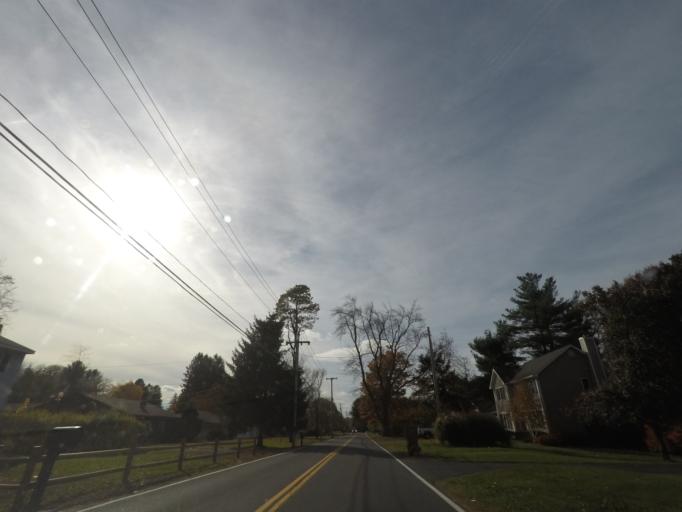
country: US
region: New York
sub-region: Schenectady County
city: Rotterdam
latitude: 42.7534
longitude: -73.9514
